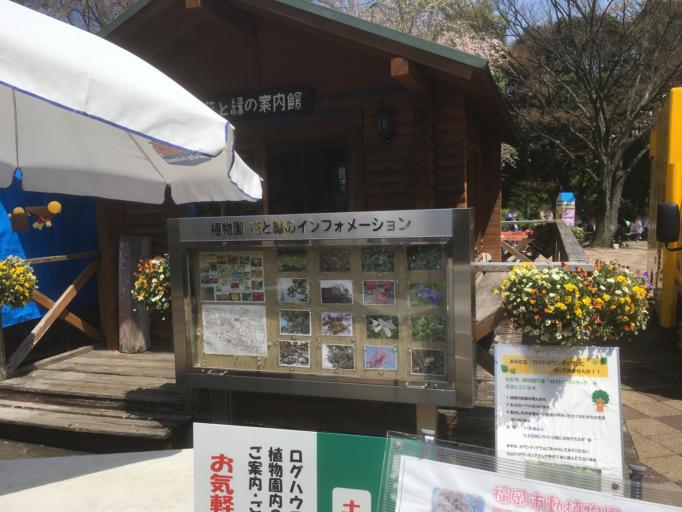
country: JP
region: Fukuoka
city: Fukuoka-shi
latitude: 33.5712
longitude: 130.3900
